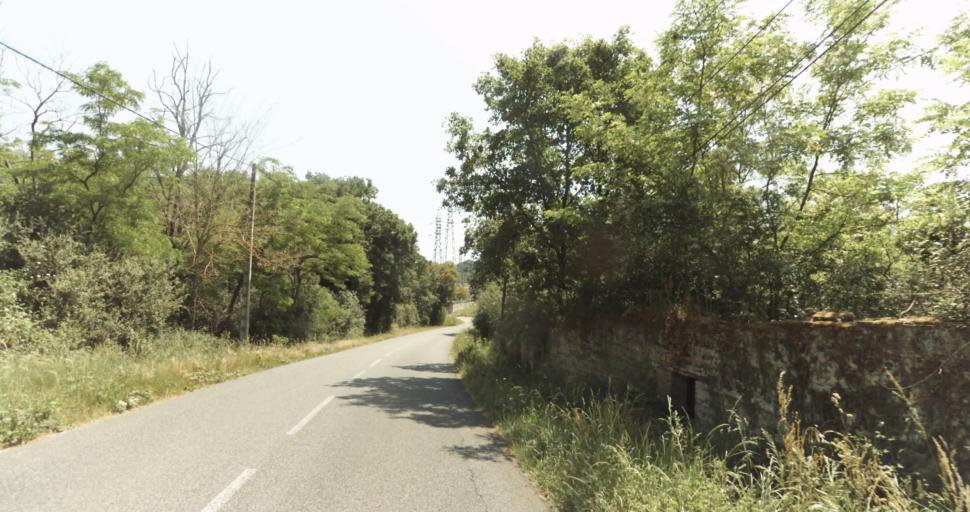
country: FR
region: Midi-Pyrenees
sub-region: Departement de la Haute-Garonne
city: La Salvetat-Saint-Gilles
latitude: 43.5982
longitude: 1.2716
